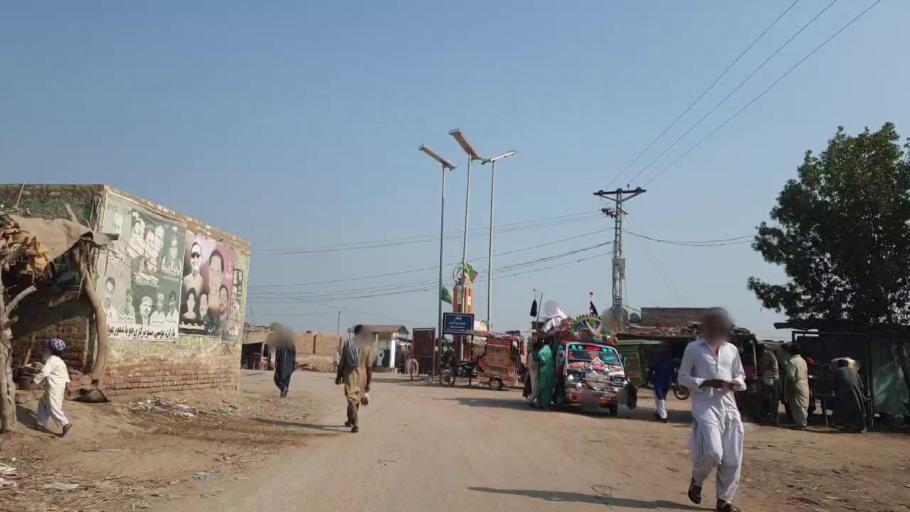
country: PK
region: Sindh
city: Matiari
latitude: 25.5009
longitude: 68.4633
